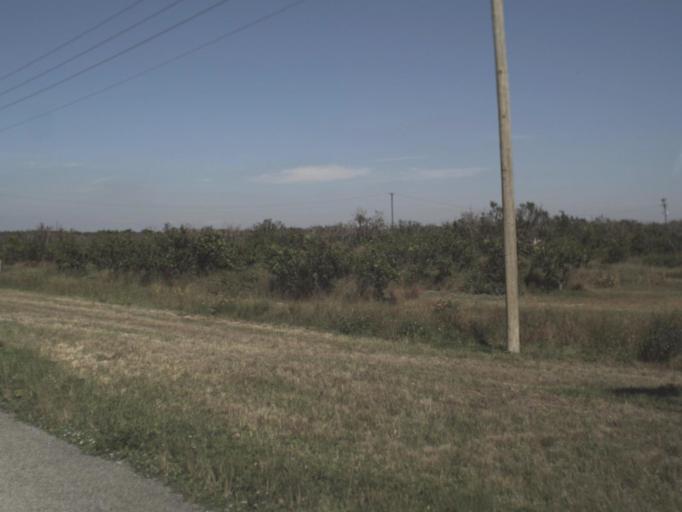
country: US
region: Florida
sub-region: Highlands County
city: Placid Lakes
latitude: 27.2105
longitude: -81.3286
